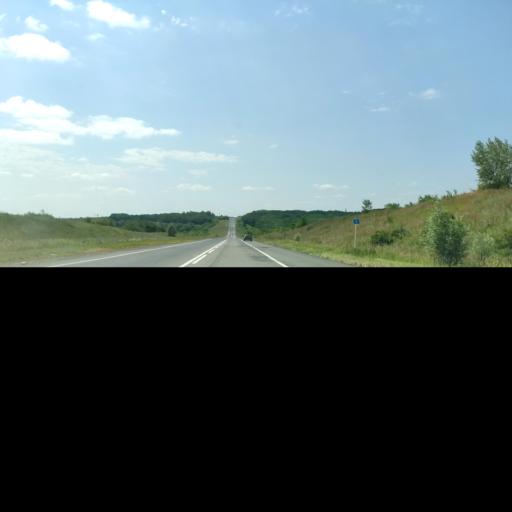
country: RU
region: Samara
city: Petra-Dubrava
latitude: 53.2972
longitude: 50.4004
